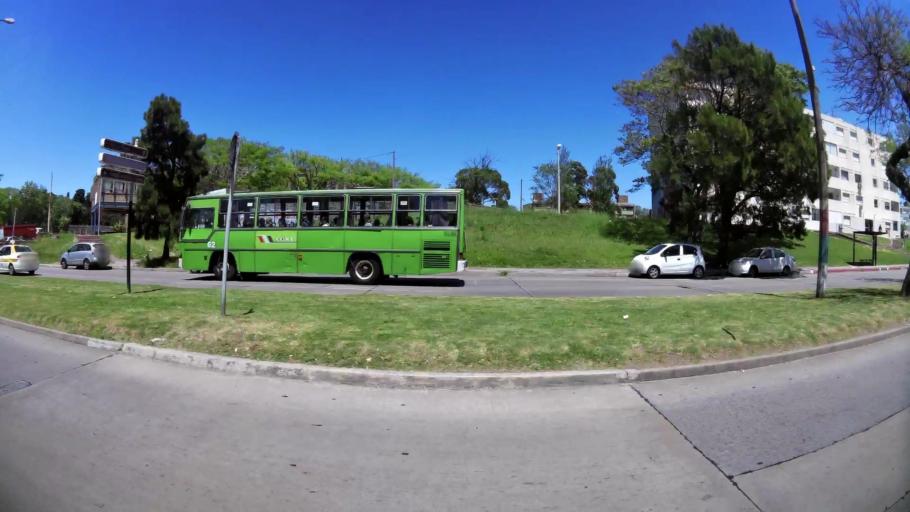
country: UY
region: Montevideo
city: Montevideo
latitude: -34.8966
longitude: -56.1257
